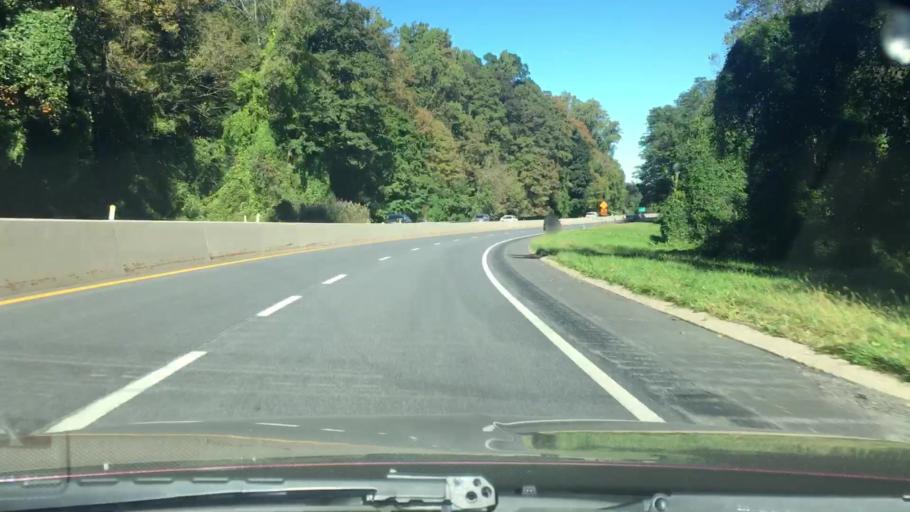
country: US
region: New York
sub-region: Westchester County
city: Chappaqua
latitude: 41.1530
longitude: -73.7808
